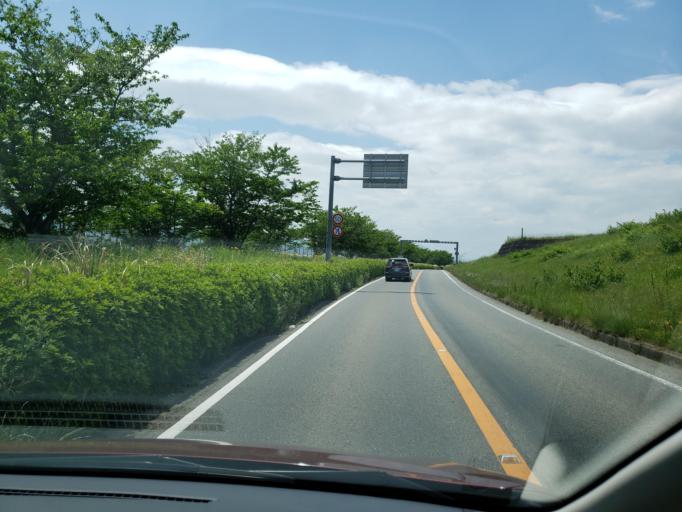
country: JP
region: Tokushima
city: Ishii
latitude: 34.1022
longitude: 134.4531
